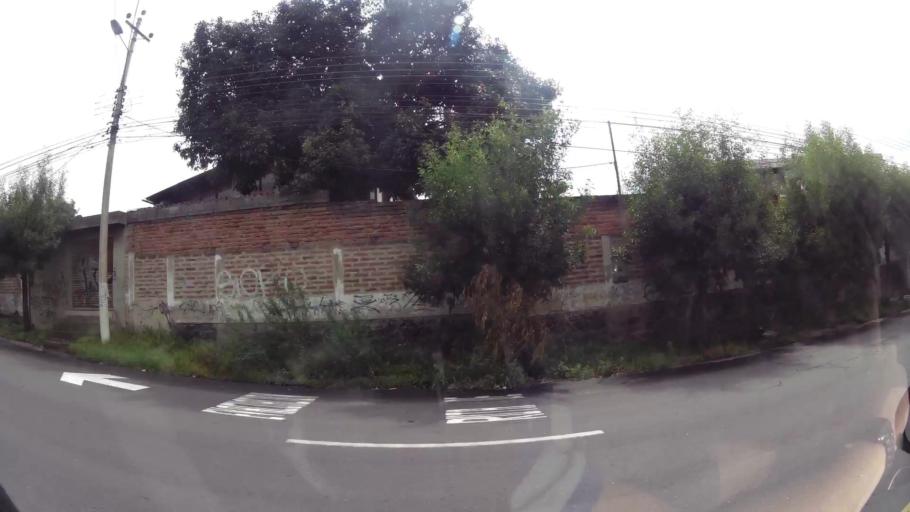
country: EC
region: Pichincha
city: Sangolqui
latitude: -0.3056
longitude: -78.4729
